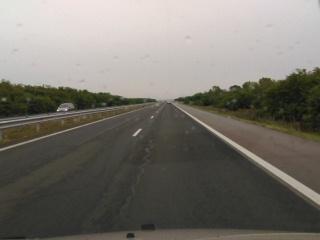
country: BG
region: Stara Zagora
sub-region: Obshtina Stara Zagora
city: Stara Zagora
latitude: 42.3439
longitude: 25.6933
